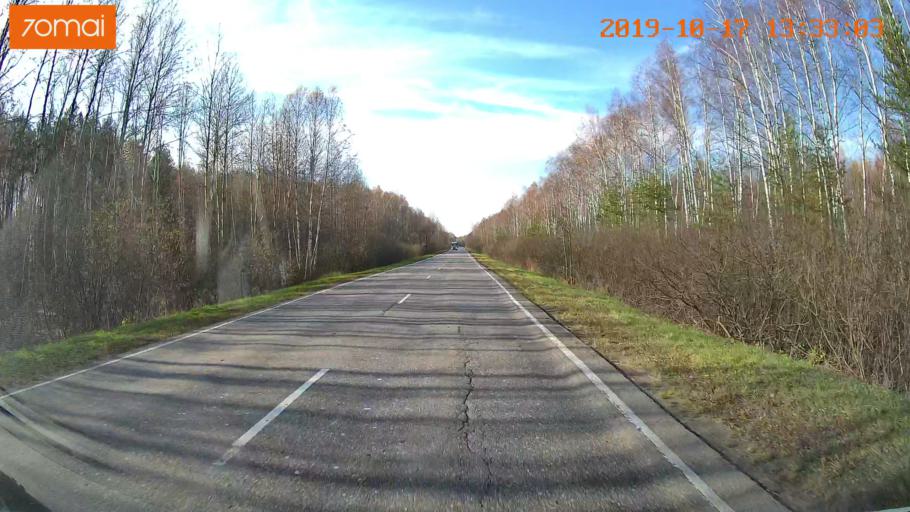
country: RU
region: Vladimir
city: Velikodvorskiy
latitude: 55.1405
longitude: 40.7503
